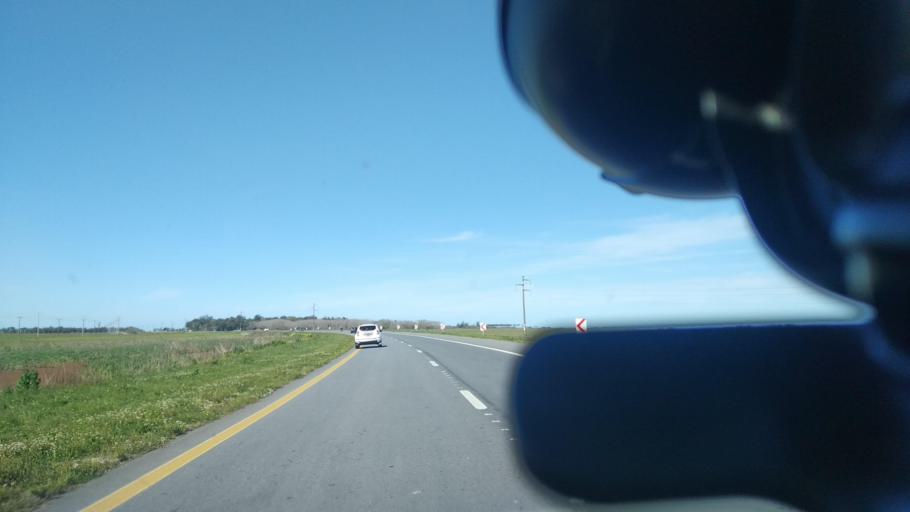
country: AR
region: Buenos Aires
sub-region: Partido de General Lavalle
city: General Lavalle
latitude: -36.4321
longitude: -56.8977
